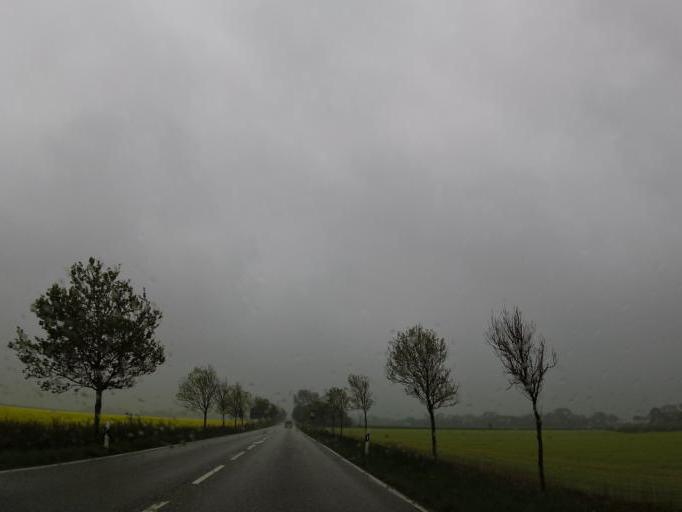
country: DE
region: Schleswig-Holstein
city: Witzwort
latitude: 54.3672
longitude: 8.9784
